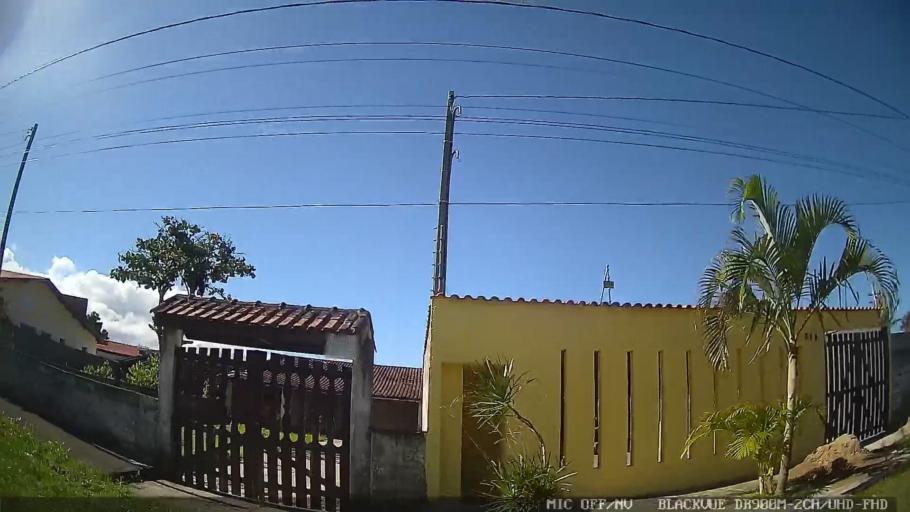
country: BR
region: Sao Paulo
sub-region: Itanhaem
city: Itanhaem
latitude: -24.2155
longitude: -46.8637
